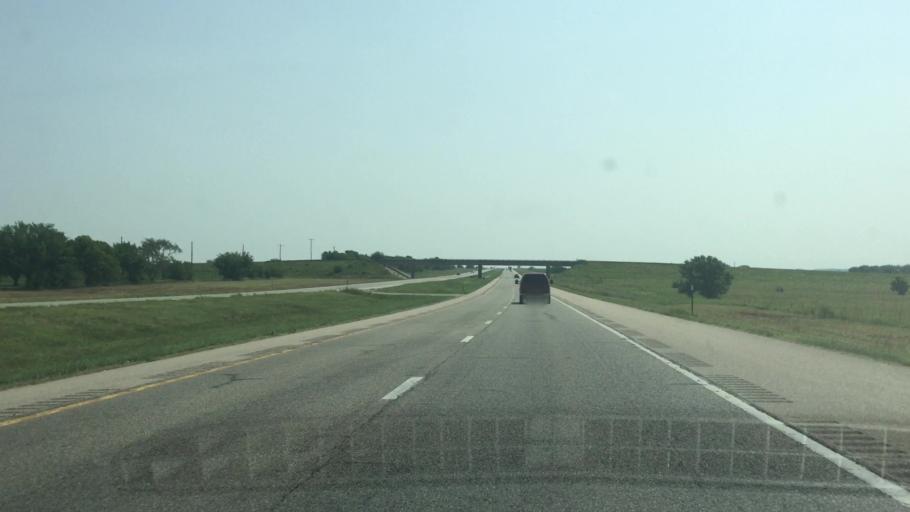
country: US
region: Kansas
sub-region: Osage County
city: Osage City
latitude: 38.4256
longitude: -95.8252
